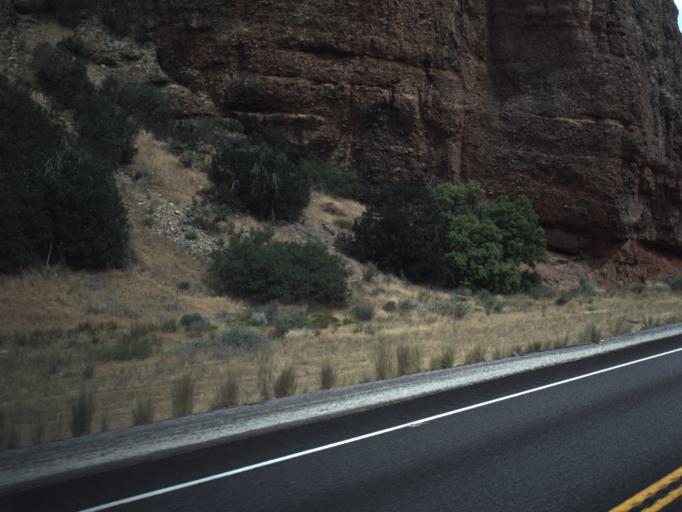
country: US
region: Utah
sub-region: Utah County
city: Mapleton
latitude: 39.9928
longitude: -111.3979
